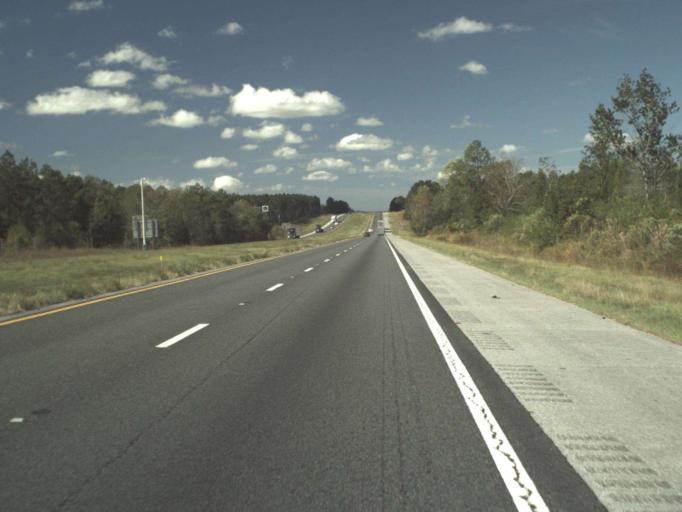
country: US
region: Florida
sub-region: Washington County
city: Chipley
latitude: 30.7510
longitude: -85.5713
